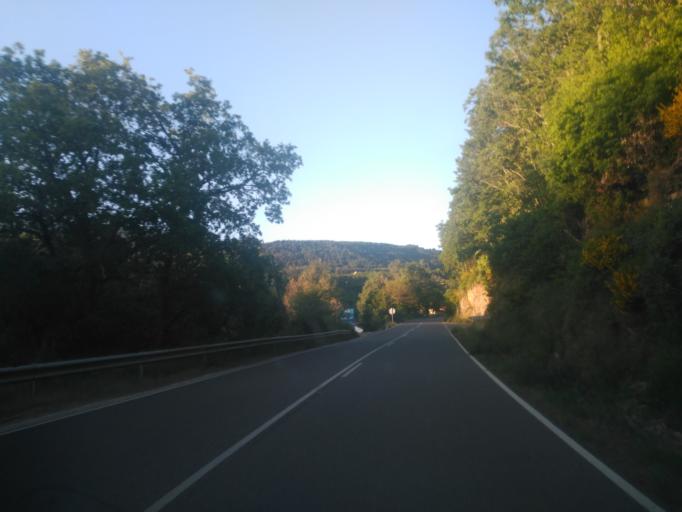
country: ES
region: Castille and Leon
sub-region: Provincia de Salamanca
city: Candelario
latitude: 40.3745
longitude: -5.7500
